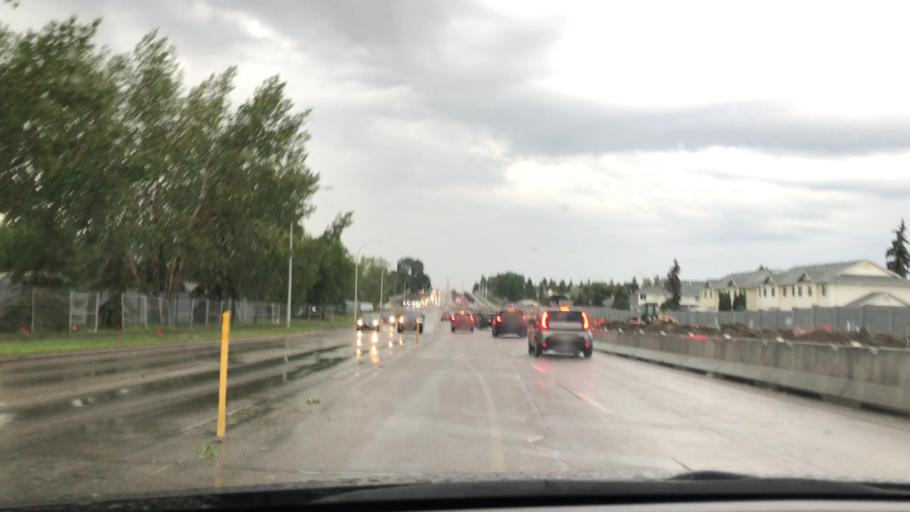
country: CA
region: Alberta
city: Edmonton
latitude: 53.4625
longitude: -113.4347
